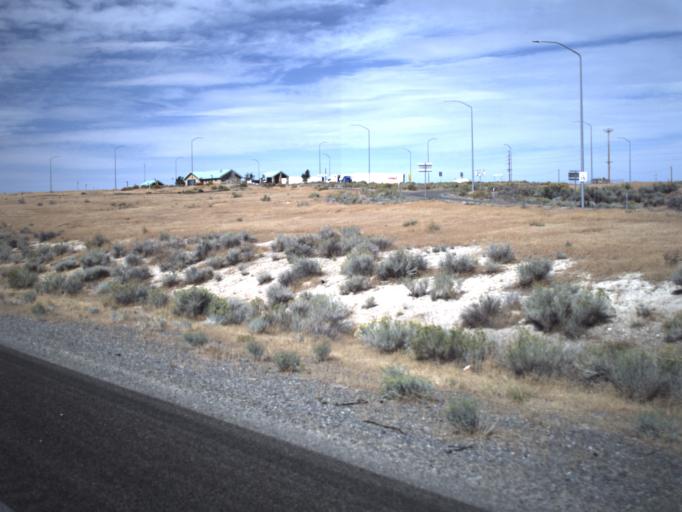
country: US
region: Utah
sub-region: Tooele County
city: Grantsville
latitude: 40.7618
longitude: -113.0069
